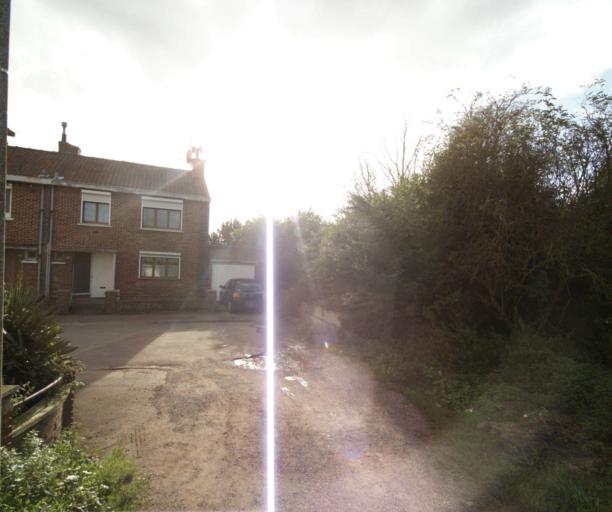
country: FR
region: Nord-Pas-de-Calais
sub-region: Departement du Nord
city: Lomme
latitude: 50.6325
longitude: 3.0009
